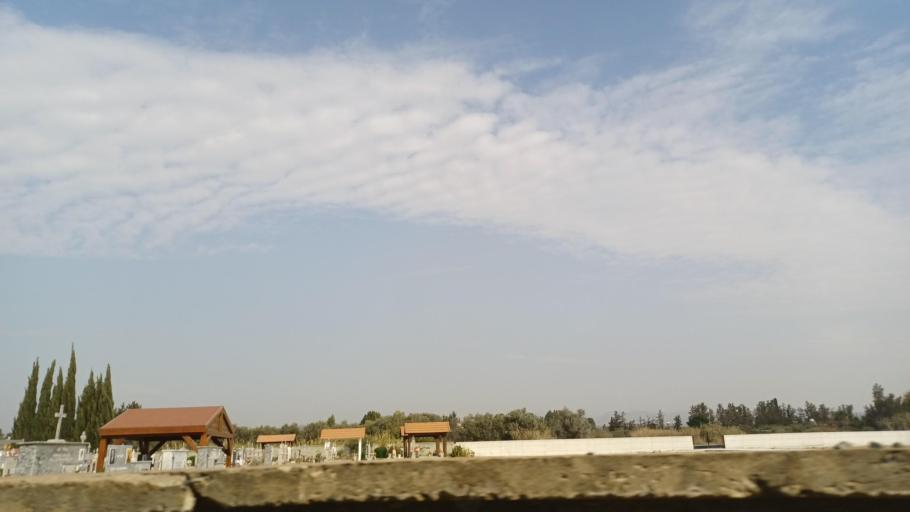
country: CY
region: Larnaka
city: Kolossi
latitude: 34.6649
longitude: 32.9459
